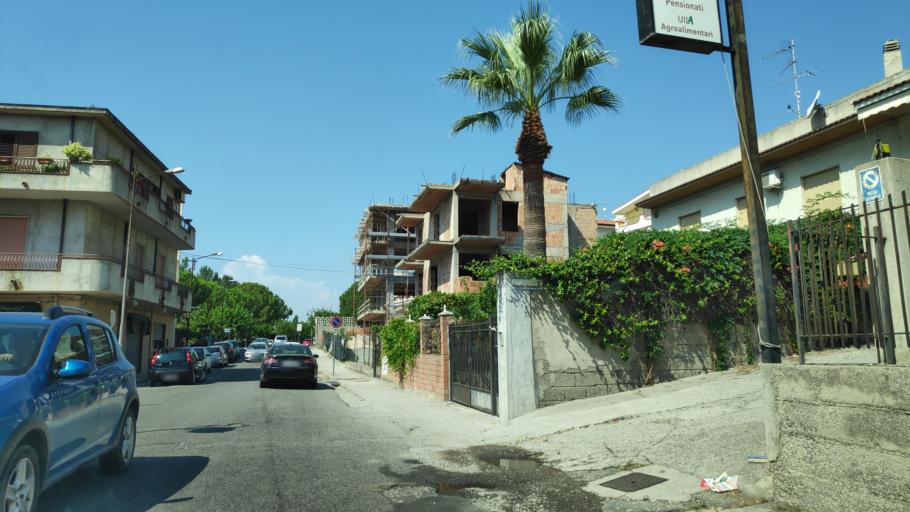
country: IT
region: Calabria
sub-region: Provincia di Reggio Calabria
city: Caulonia Marina
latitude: 38.3453
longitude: 16.4657
